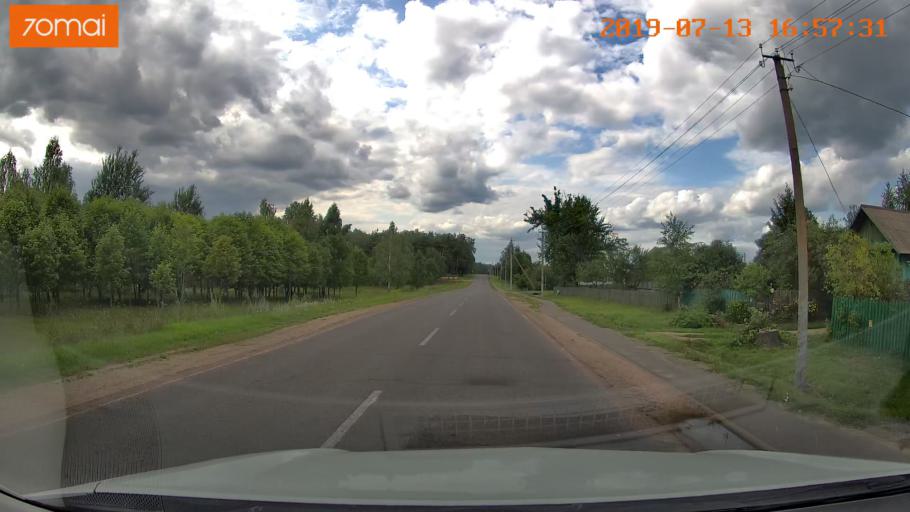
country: BY
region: Mogilev
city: Kirawsk
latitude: 53.2805
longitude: 29.4508
